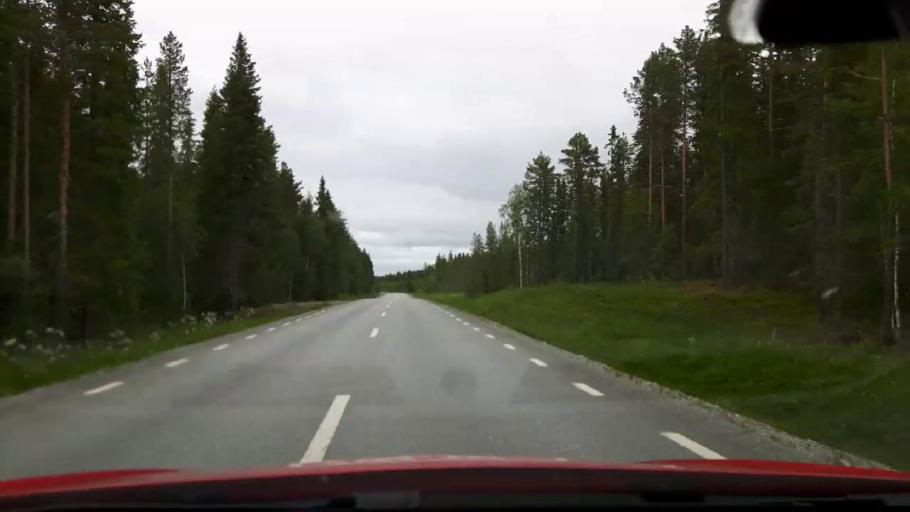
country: SE
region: Jaemtland
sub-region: OEstersunds Kommun
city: Lit
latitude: 63.7038
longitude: 14.6888
